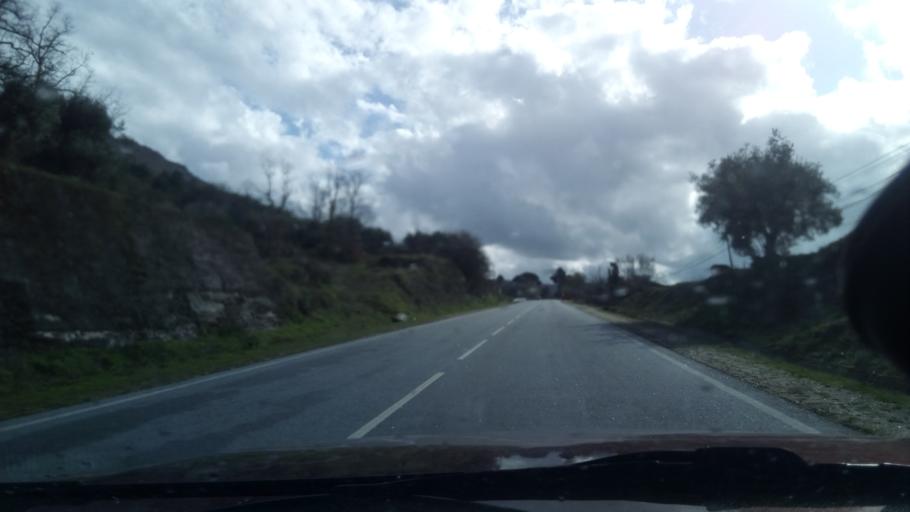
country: PT
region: Guarda
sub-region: Guarda
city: Guarda
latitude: 40.5859
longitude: -7.2913
